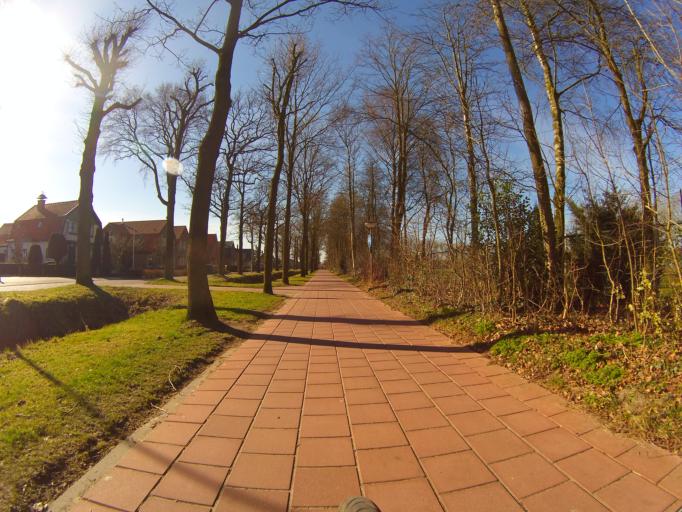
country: NL
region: Utrecht
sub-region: Gemeente Utrechtse Heuvelrug
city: Overberg
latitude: 52.0834
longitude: 5.4869
